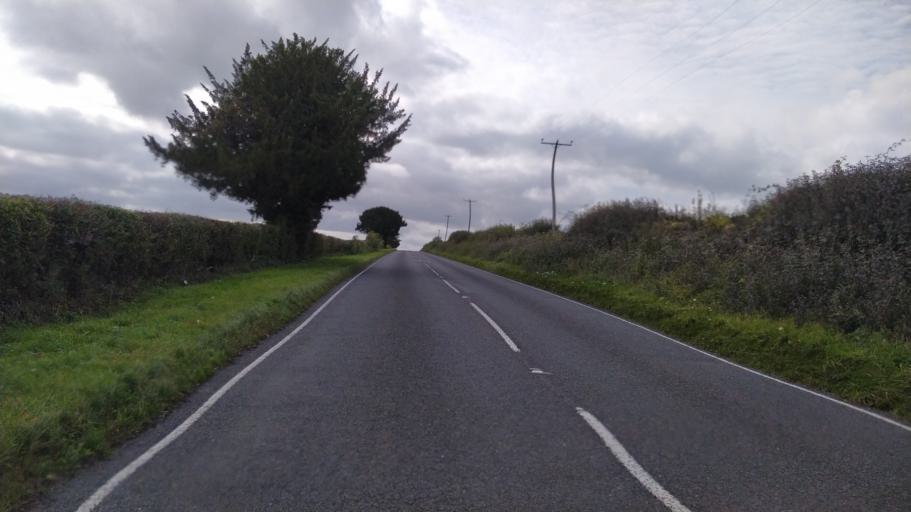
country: GB
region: England
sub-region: Hampshire
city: Andover
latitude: 51.1250
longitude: -1.4325
